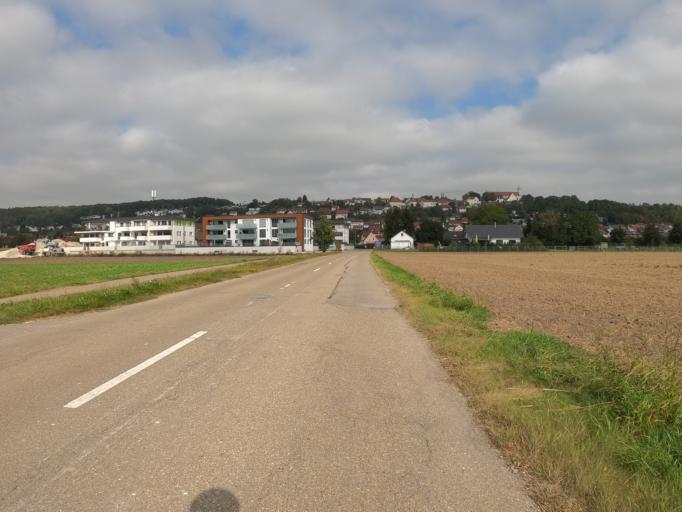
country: DE
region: Bavaria
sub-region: Swabia
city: Nersingen
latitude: 48.4453
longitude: 10.0877
